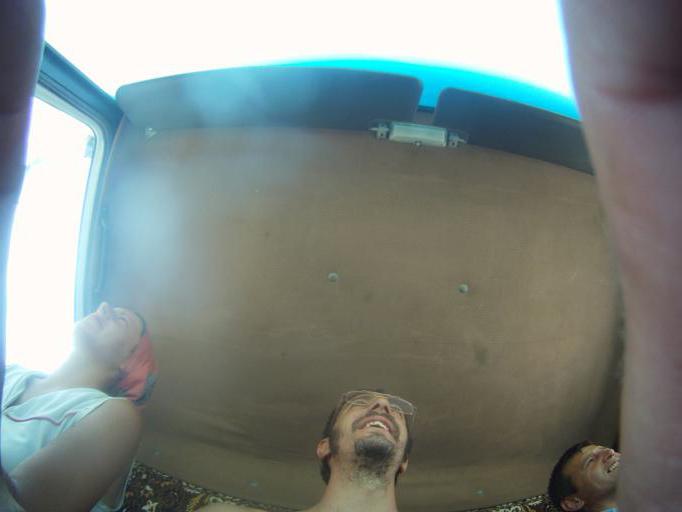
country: KZ
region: Ongtustik Qazaqstan
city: Shayan
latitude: 42.9796
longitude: 68.8450
